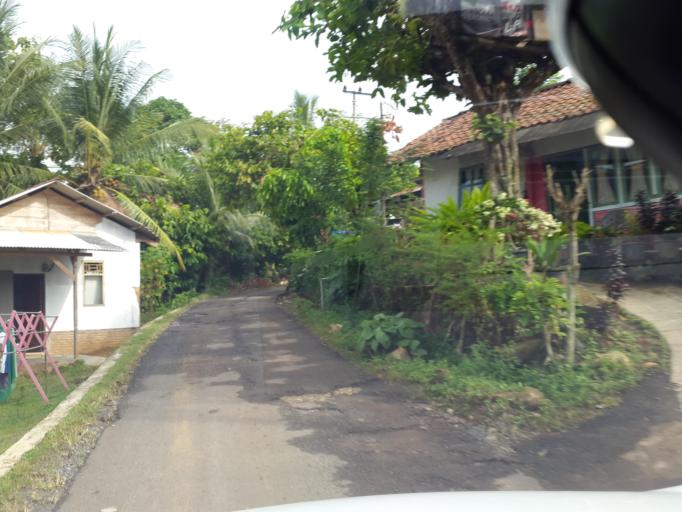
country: ID
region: Lampung
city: Kedaton
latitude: -5.3914
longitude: 105.1929
